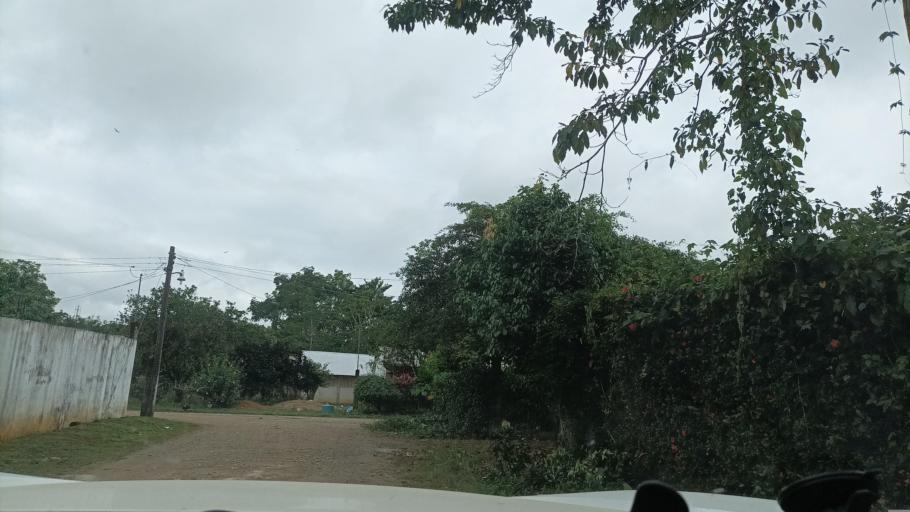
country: MX
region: Veracruz
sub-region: Uxpanapa
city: Poblado 10
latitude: 17.2703
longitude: -94.4999
